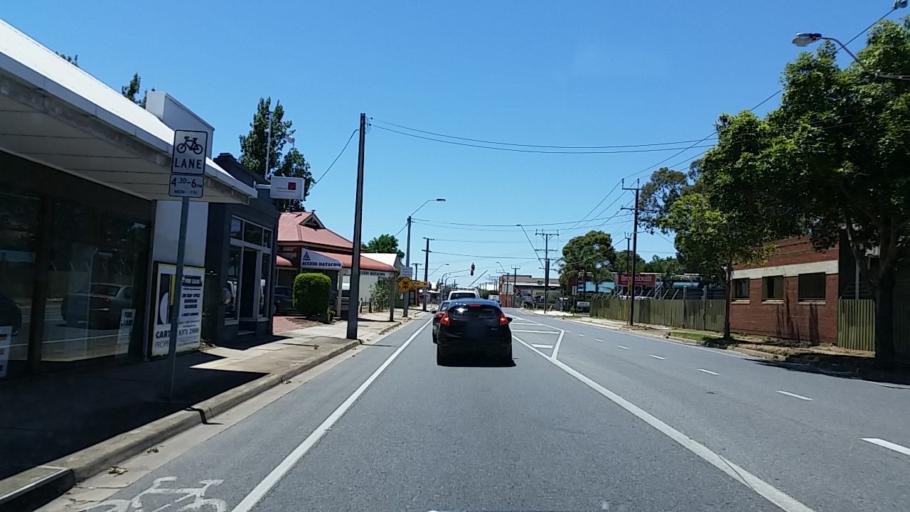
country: AU
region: South Australia
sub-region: Charles Sturt
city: Woodville
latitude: -34.8870
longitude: 138.5487
